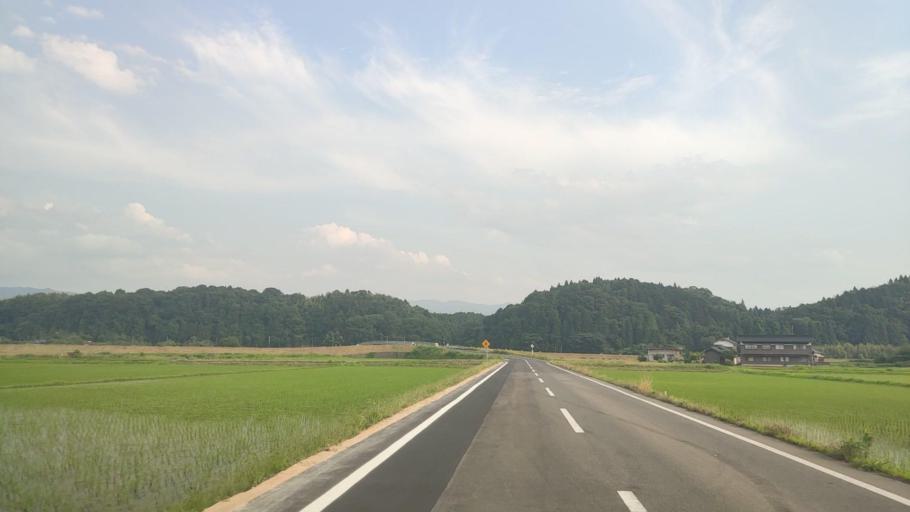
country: JP
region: Tottori
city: Kurayoshi
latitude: 35.4199
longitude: 133.7815
